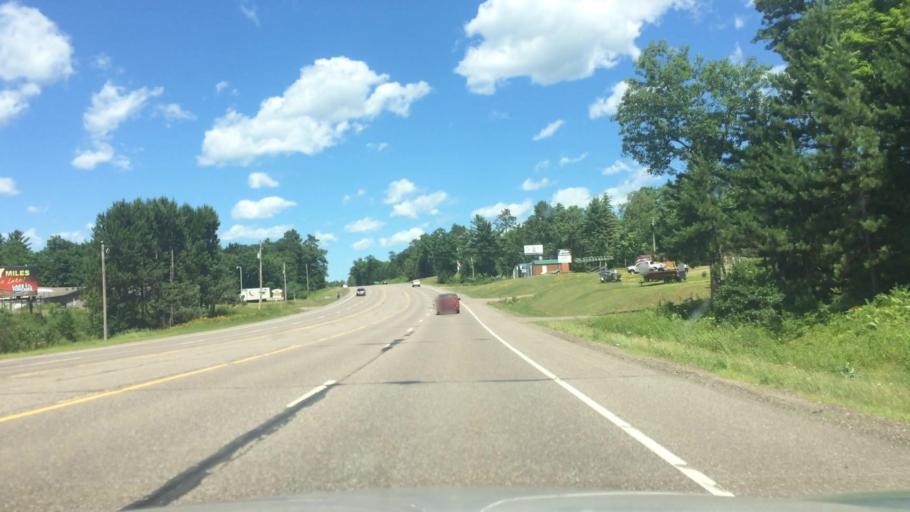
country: US
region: Wisconsin
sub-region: Vilas County
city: Lac du Flambeau
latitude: 45.8367
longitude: -89.7104
